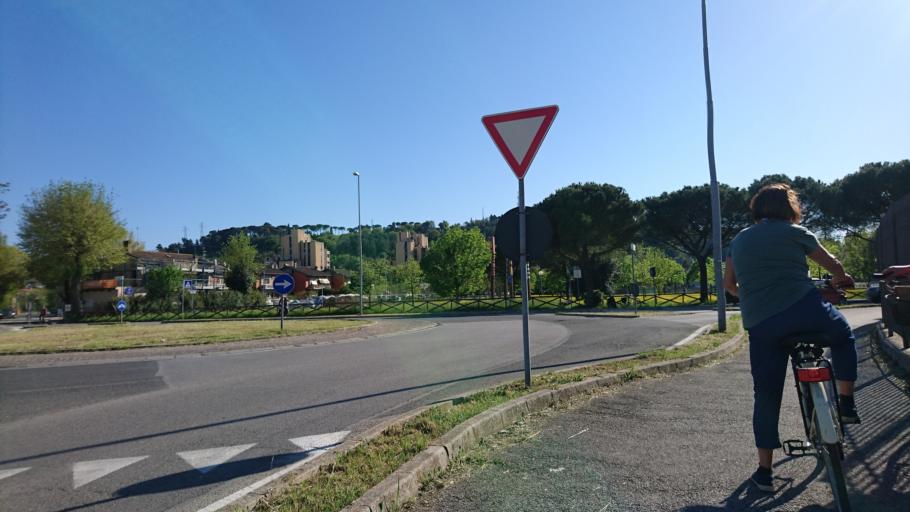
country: IT
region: The Marches
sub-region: Provincia di Pesaro e Urbino
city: Pesaro
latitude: 43.8922
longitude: 12.8990
